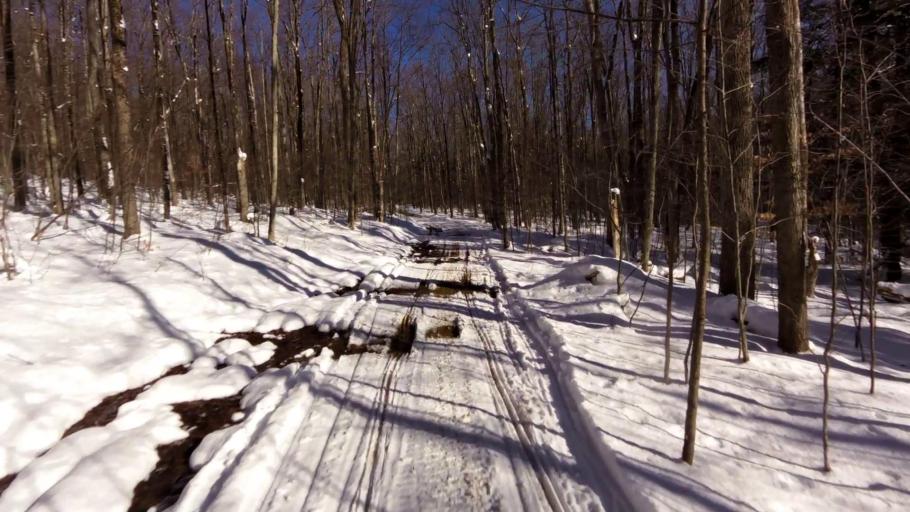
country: US
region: New York
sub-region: Cattaraugus County
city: Salamanca
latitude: 42.0207
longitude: -78.7897
